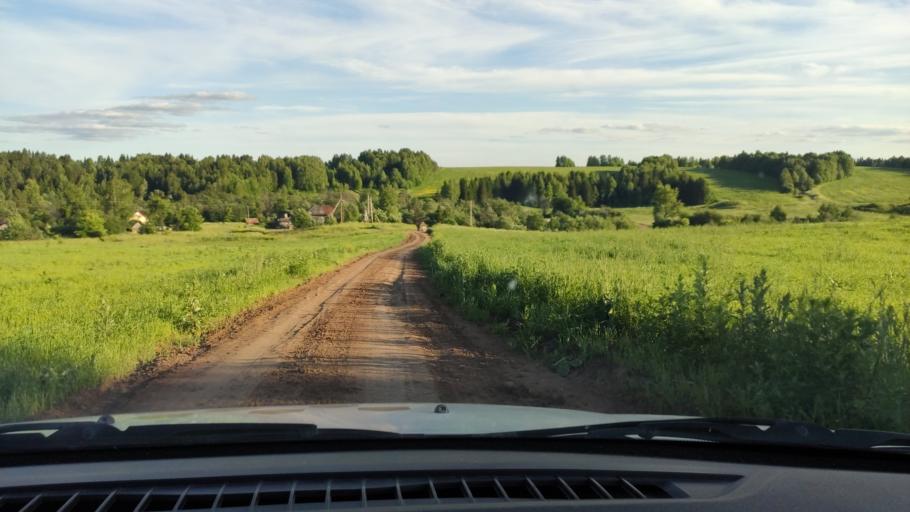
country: RU
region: Perm
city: Orda
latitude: 57.2932
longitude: 56.5941
